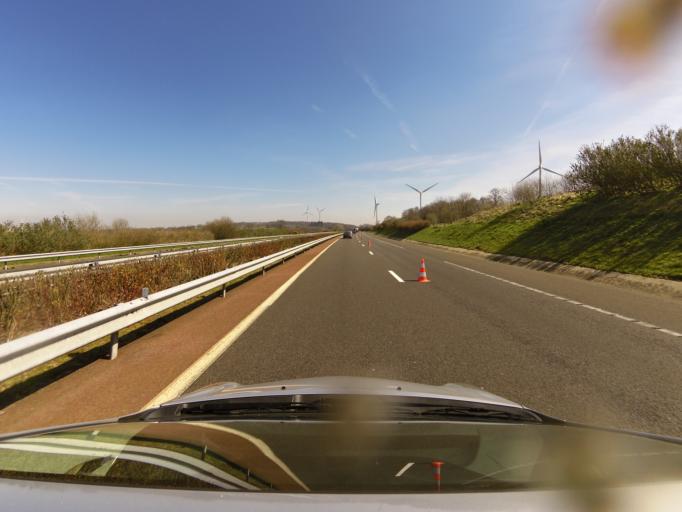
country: FR
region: Lower Normandy
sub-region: Departement de la Manche
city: Percy
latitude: 48.8942
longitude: -1.1272
